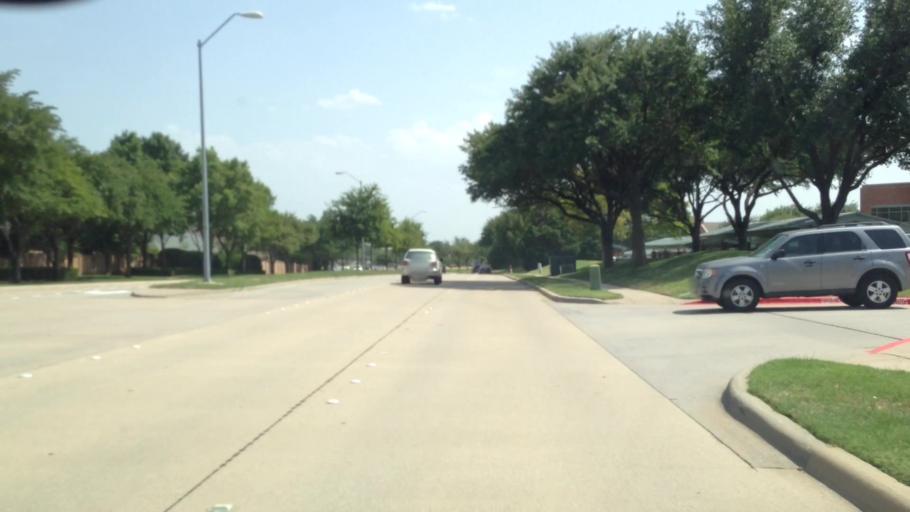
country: US
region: Texas
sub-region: Dallas County
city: Addison
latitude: 33.0388
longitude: -96.8274
